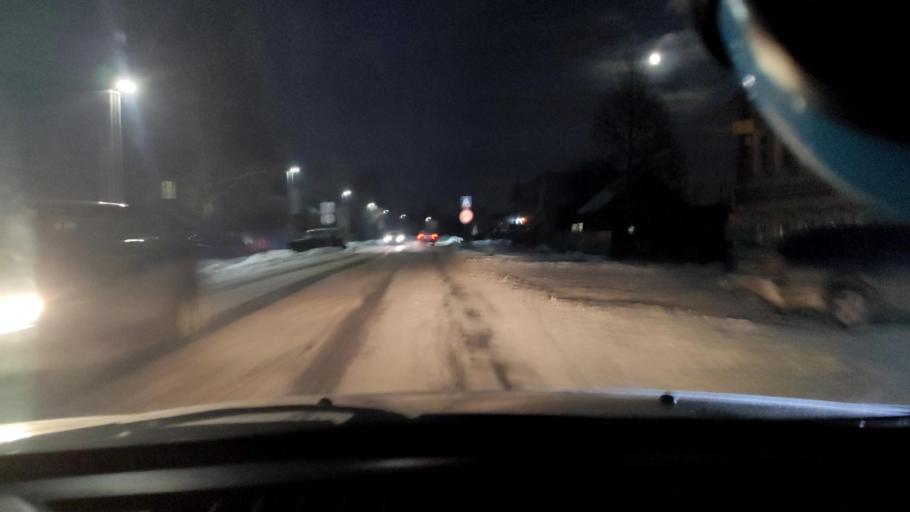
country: RU
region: Perm
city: Kultayevo
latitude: 57.8939
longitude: 55.9351
